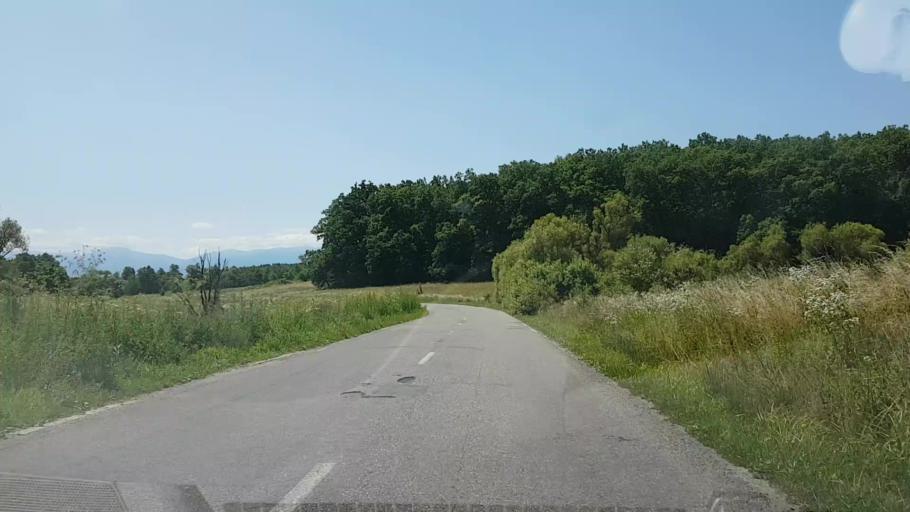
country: RO
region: Brasov
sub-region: Comuna Cincu
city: Cincu
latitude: 45.8827
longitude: 24.8137
